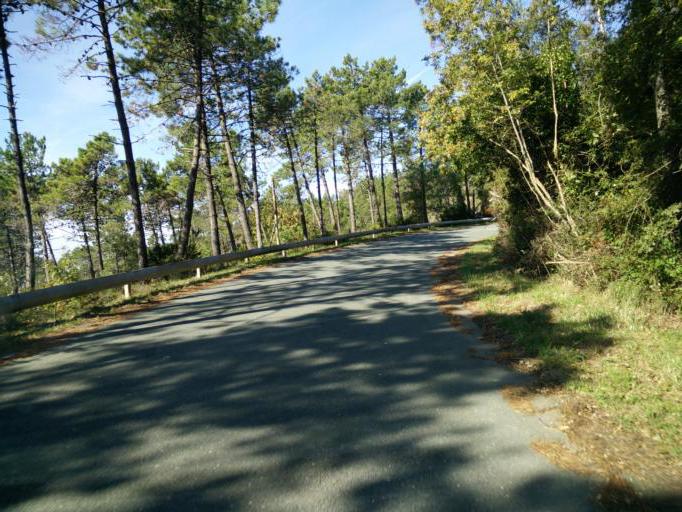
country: IT
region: Liguria
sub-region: Provincia di La Spezia
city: Framura
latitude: 44.2340
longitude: 9.5785
